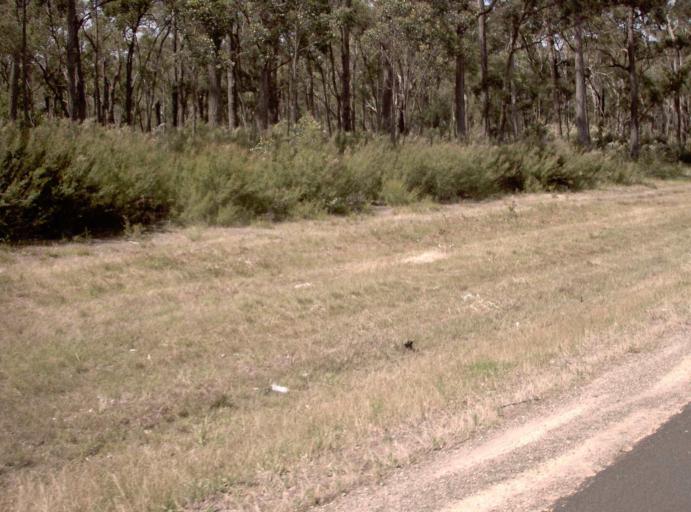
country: AU
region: Victoria
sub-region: Wellington
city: Sale
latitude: -37.9220
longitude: 147.2467
